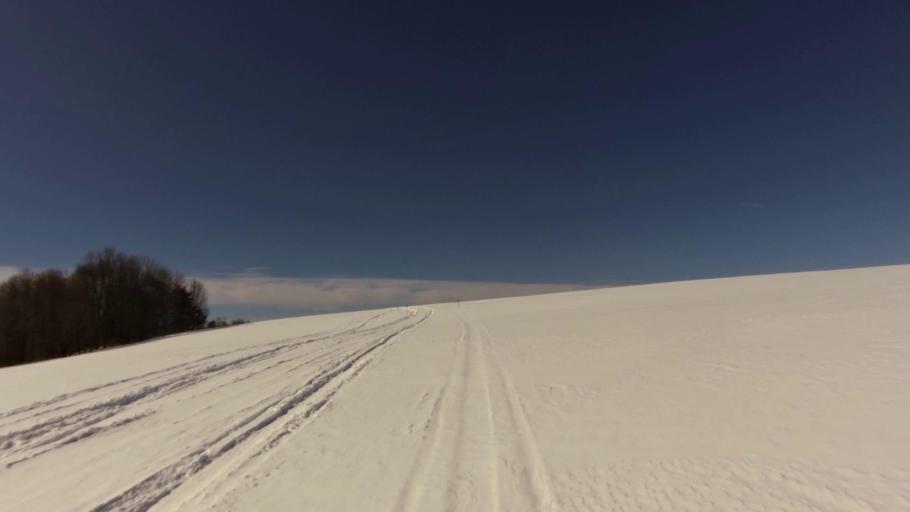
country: US
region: New York
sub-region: Allegany County
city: Cuba
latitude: 42.3123
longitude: -78.2794
